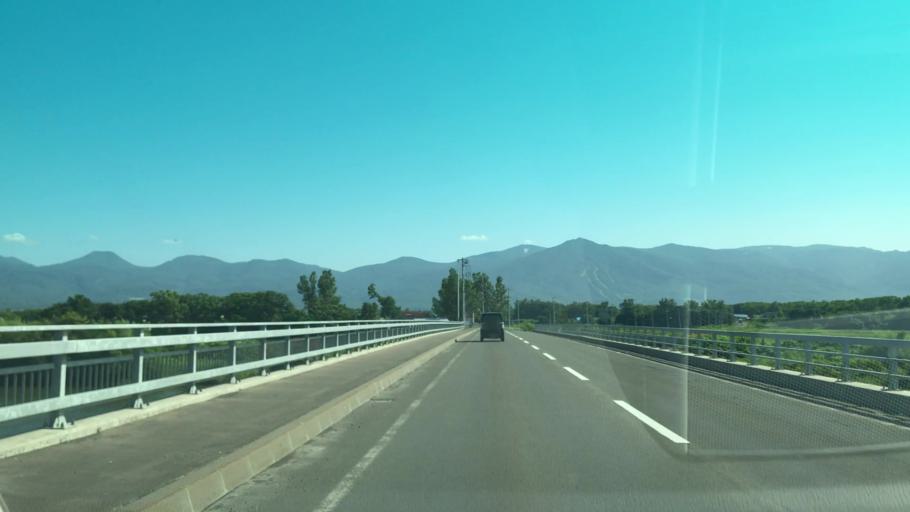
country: JP
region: Hokkaido
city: Iwanai
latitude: 43.0224
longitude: 140.5482
